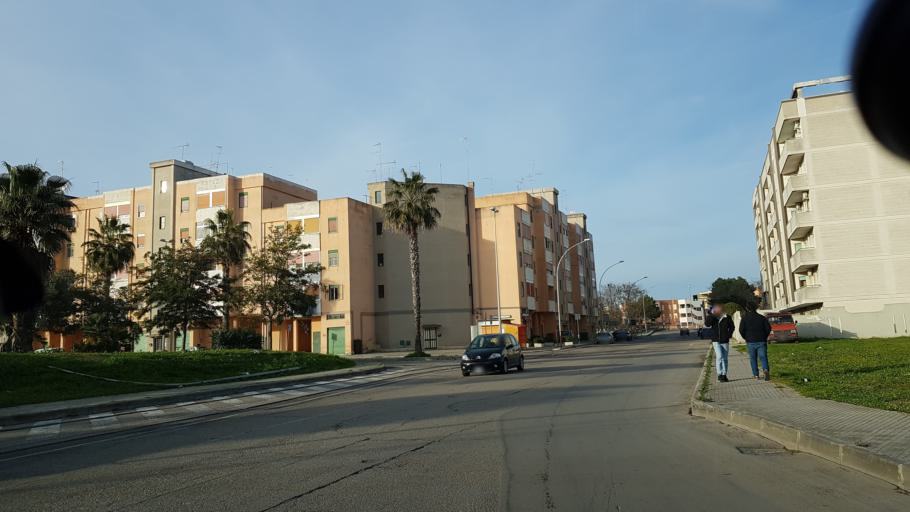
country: IT
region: Apulia
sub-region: Provincia di Brindisi
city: Brindisi
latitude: 40.6185
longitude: 17.9332
